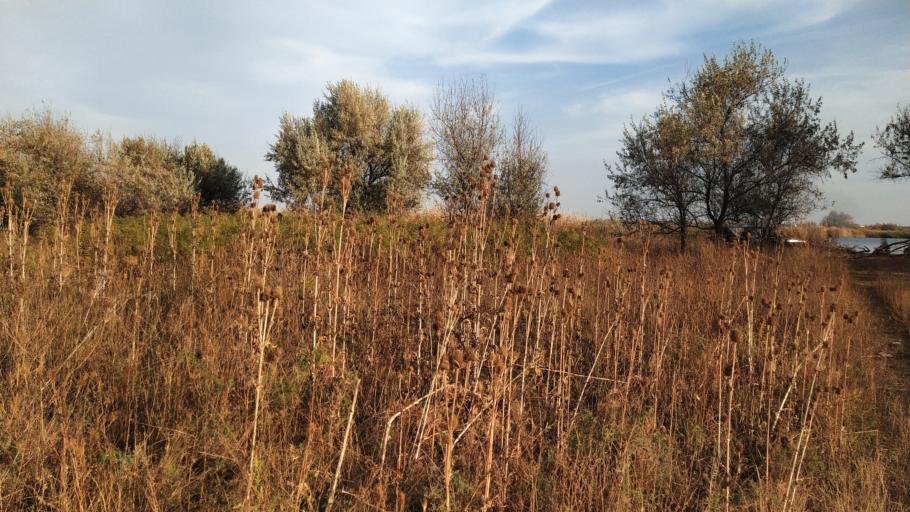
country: RU
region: Rostov
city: Kuleshovka
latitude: 47.1253
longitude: 39.6280
